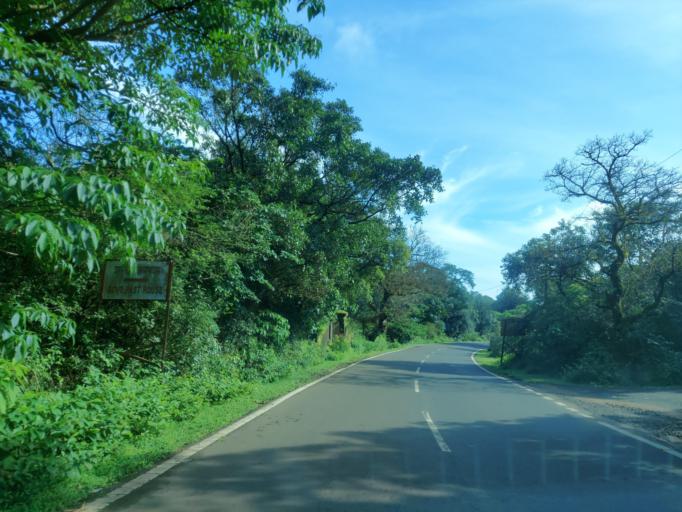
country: IN
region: Maharashtra
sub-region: Sindhudurg
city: Savantvadi
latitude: 15.9605
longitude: 73.9948
